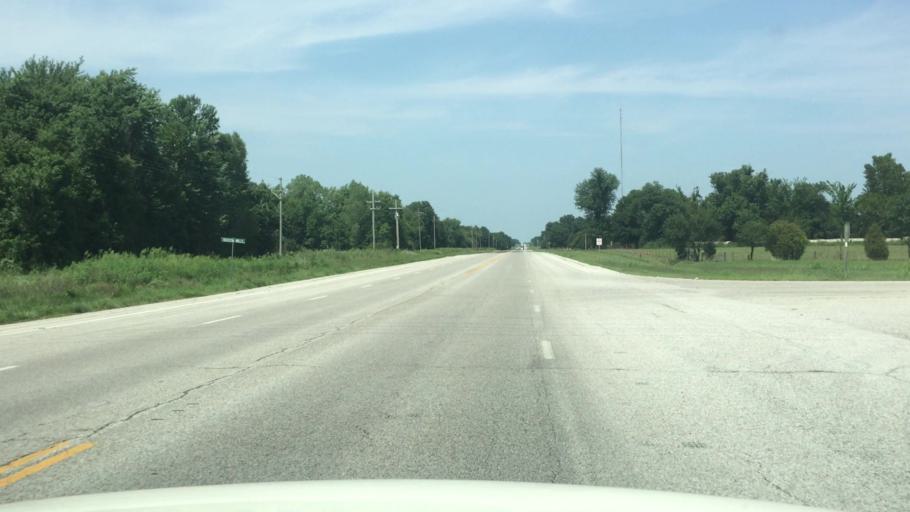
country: US
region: Kansas
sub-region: Cherokee County
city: Galena
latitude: 37.1209
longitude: -94.7043
